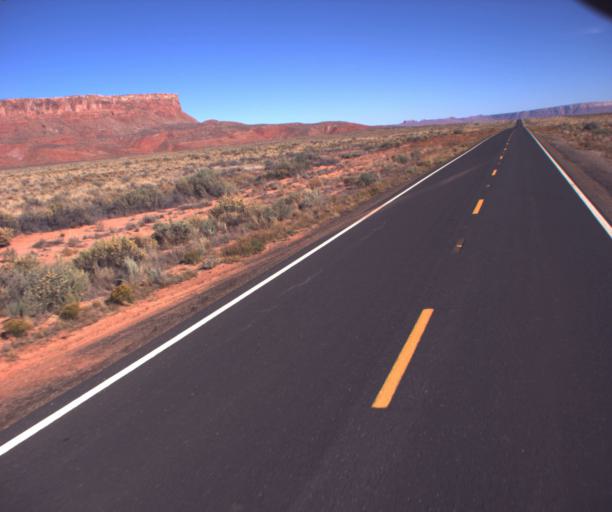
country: US
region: Arizona
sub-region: Coconino County
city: Page
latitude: 36.6961
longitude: -111.9092
